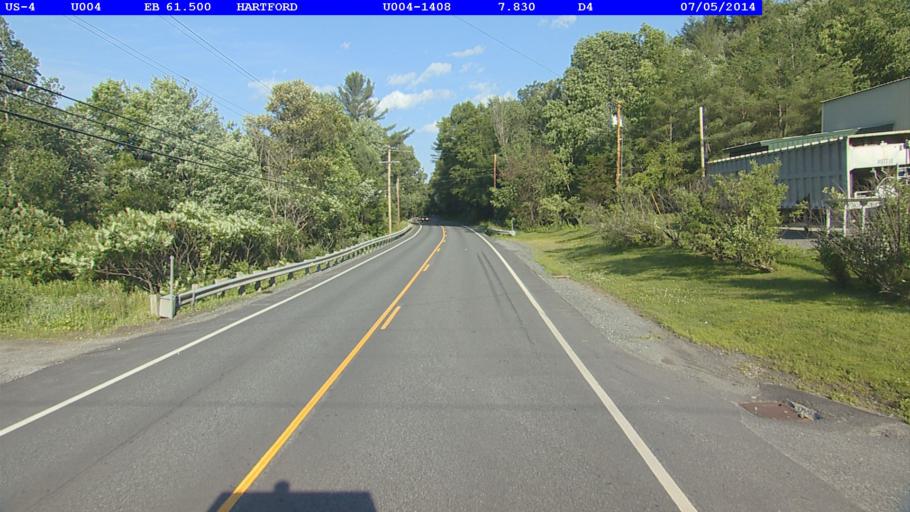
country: US
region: Vermont
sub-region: Windsor County
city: White River Junction
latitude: 43.6615
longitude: -72.3560
